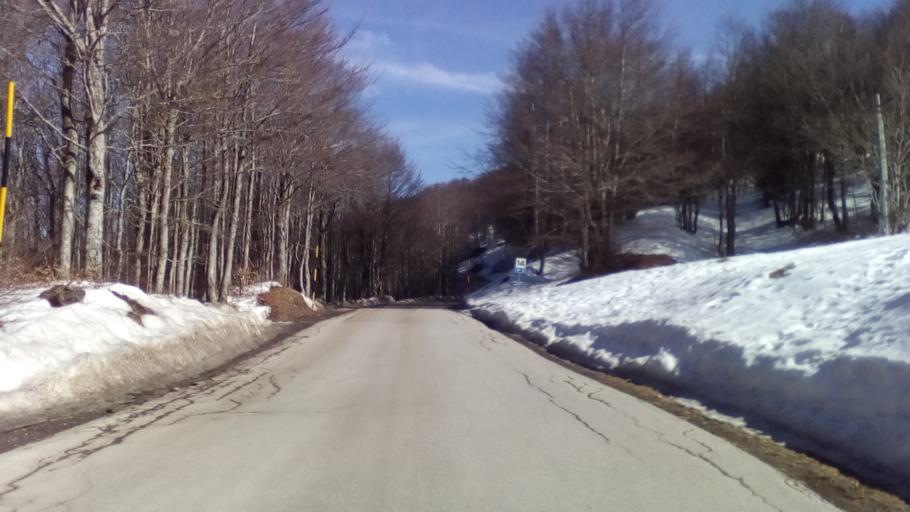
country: IT
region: Tuscany
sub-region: Provincia di Lucca
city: Castiglione di Garfagnana
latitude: 44.1981
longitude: 10.4864
